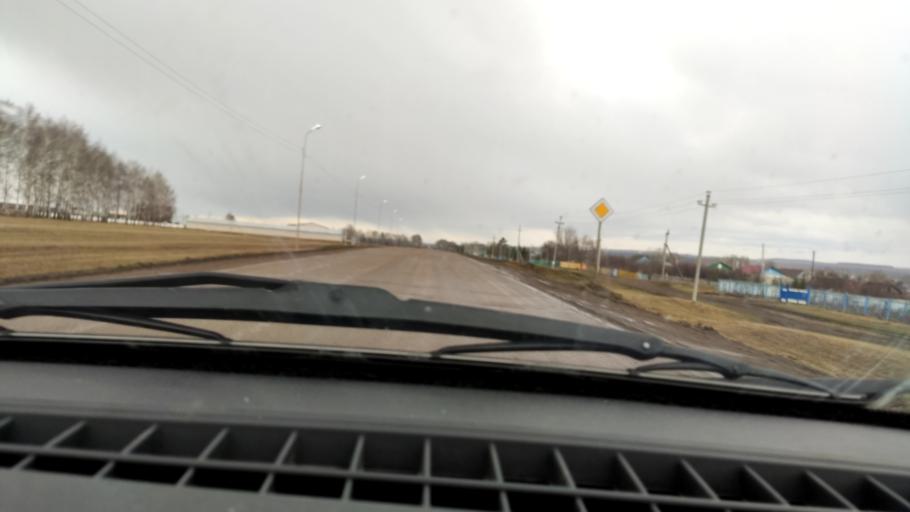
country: RU
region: Bashkortostan
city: Chekmagush
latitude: 55.1167
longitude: 54.8311
